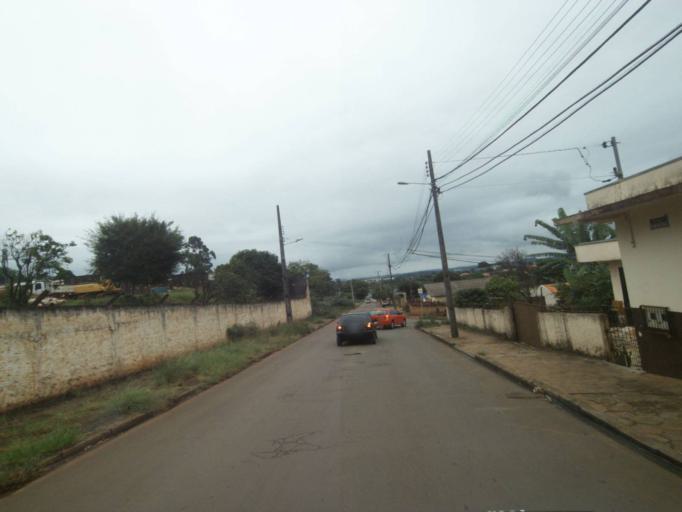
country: BR
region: Parana
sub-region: Telemaco Borba
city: Telemaco Borba
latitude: -24.3303
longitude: -50.6470
